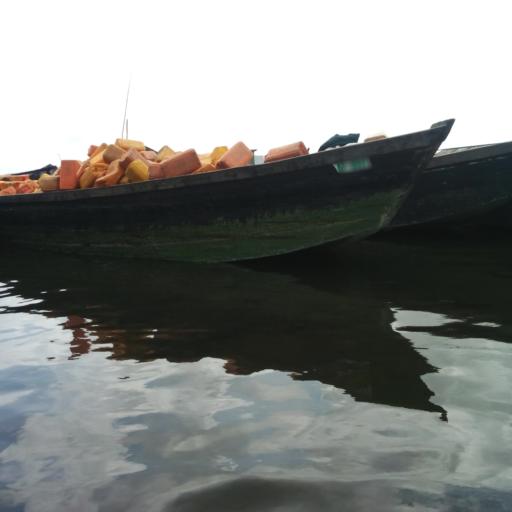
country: BJ
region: Littoral
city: Cotonou
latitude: 6.3937
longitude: 2.4277
